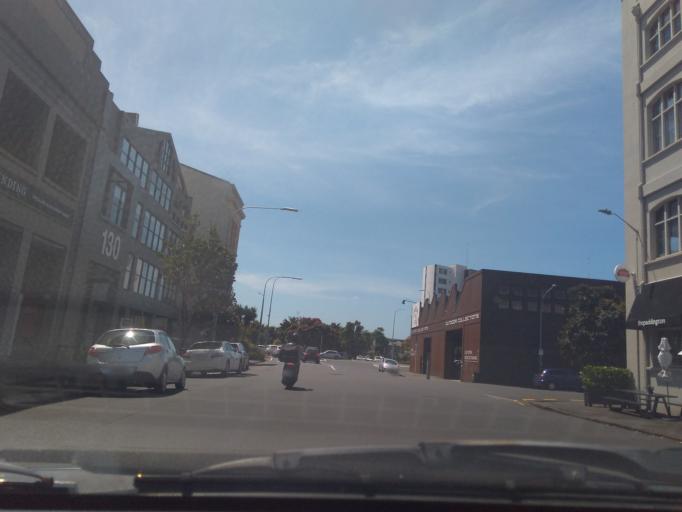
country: NZ
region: Auckland
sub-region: Auckland
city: Auckland
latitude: -36.8508
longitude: 174.7823
